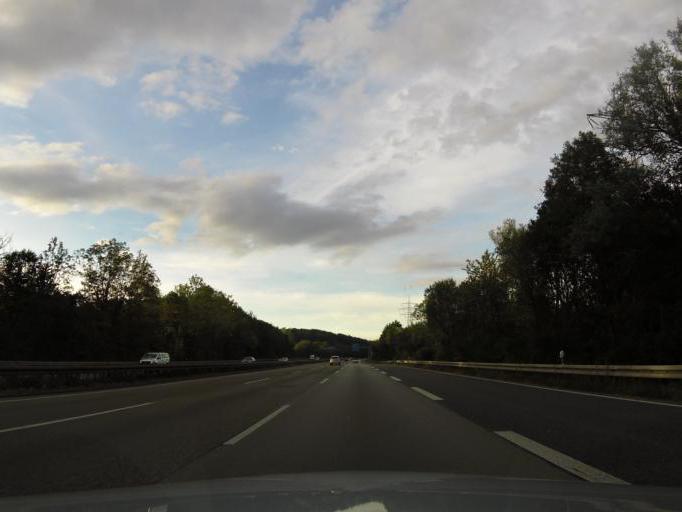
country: DE
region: Hesse
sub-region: Regierungsbezirk Darmstadt
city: Offenbach
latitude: 50.0814
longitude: 8.7369
